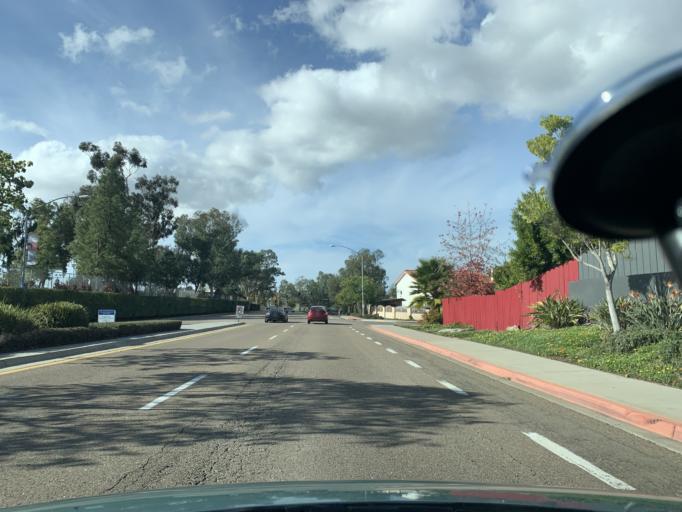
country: US
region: California
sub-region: San Diego County
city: San Diego
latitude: 32.7929
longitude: -117.1684
